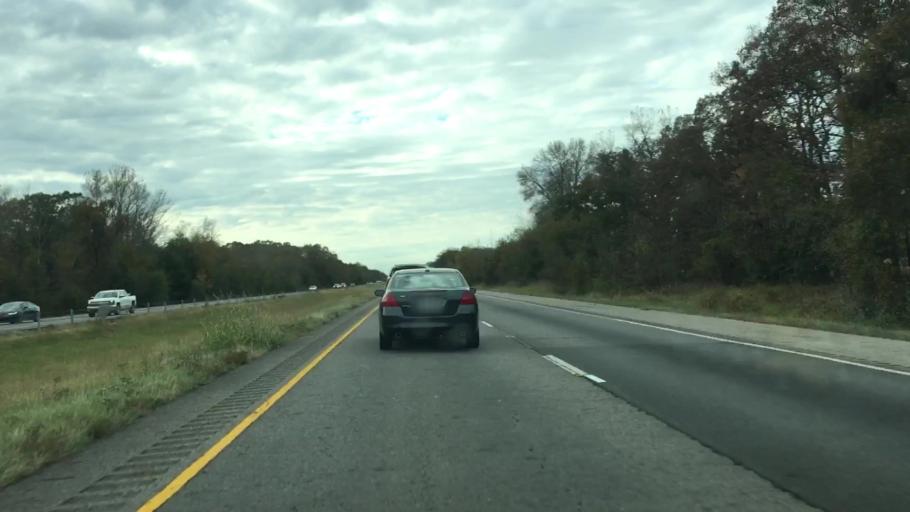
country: US
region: Arkansas
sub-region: Conway County
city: Morrilton
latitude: 35.1610
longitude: -92.5983
